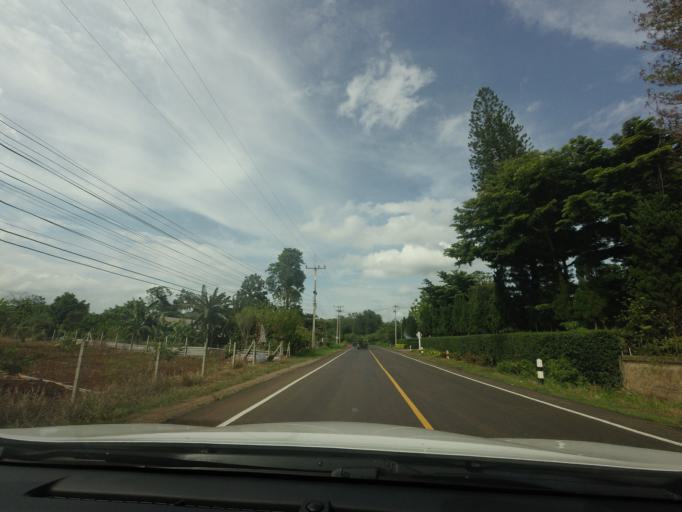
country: TH
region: Nakhon Ratchasima
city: Pak Chong
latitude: 14.5473
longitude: 101.4481
